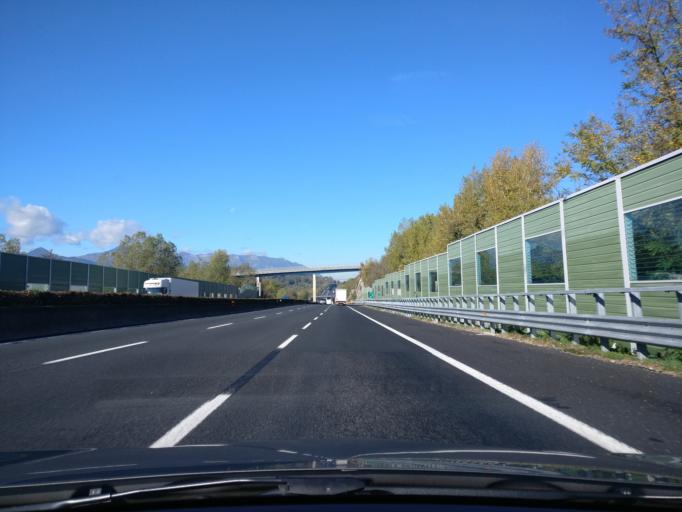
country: IT
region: Latium
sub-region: Provincia di Frosinone
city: Arnara
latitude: 41.5727
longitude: 13.3779
